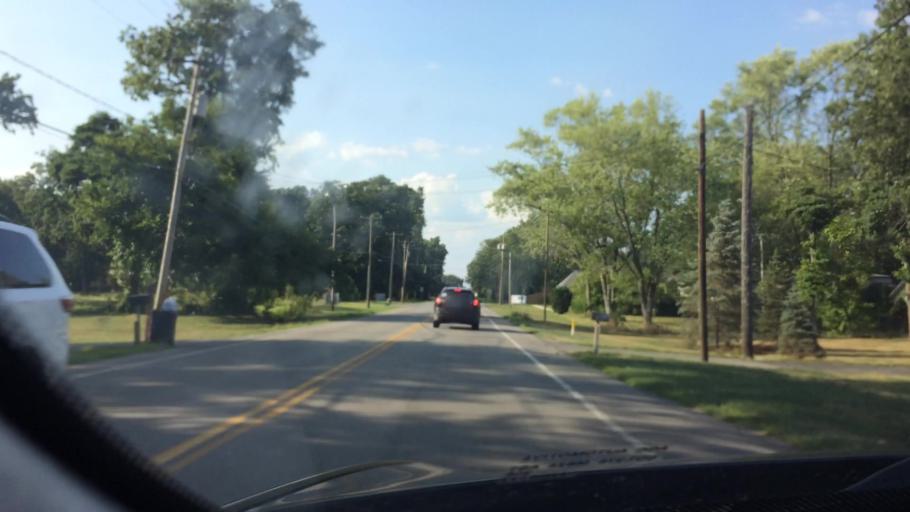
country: US
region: Ohio
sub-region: Lucas County
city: Holland
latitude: 41.6674
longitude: -83.7225
